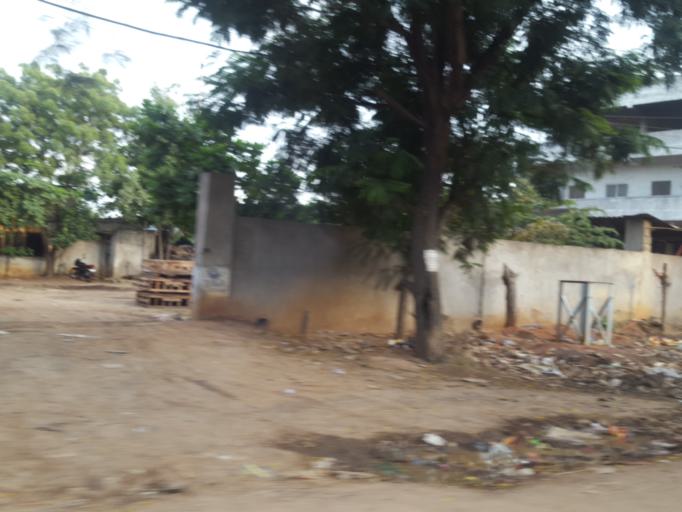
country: IN
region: Telangana
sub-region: Rangareddi
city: Quthbullapur
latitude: 17.5777
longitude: 78.4251
